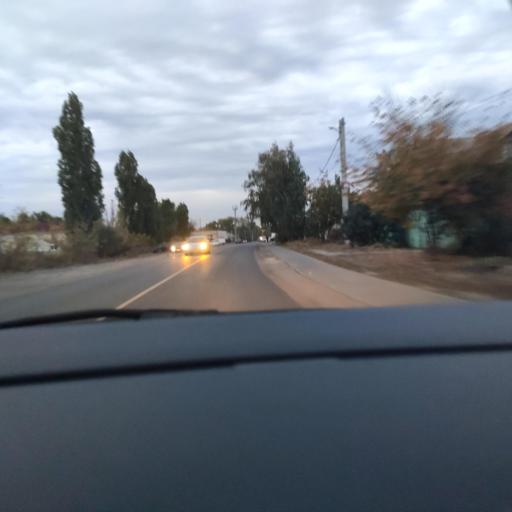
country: RU
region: Voronezj
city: Podgornoye
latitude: 51.7310
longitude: 39.1378
